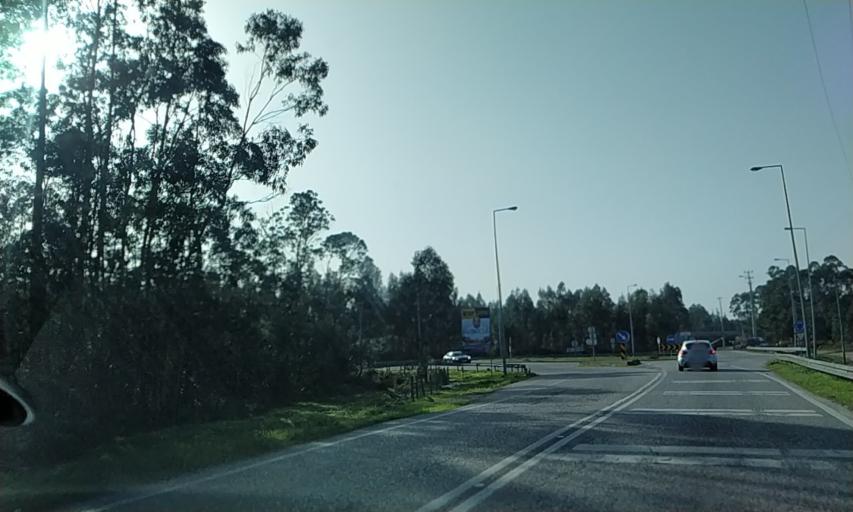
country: PT
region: Leiria
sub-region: Marinha Grande
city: Marinha Grande
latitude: 39.7456
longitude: -8.8766
